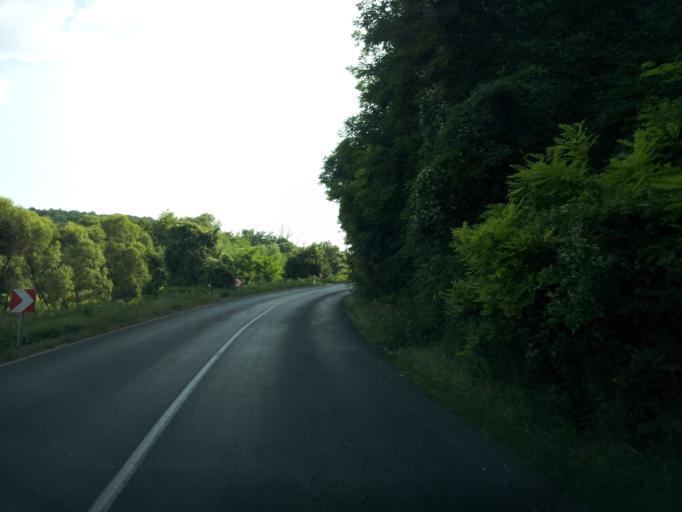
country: HU
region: Veszprem
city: Revfueloep
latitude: 46.9325
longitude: 17.5701
